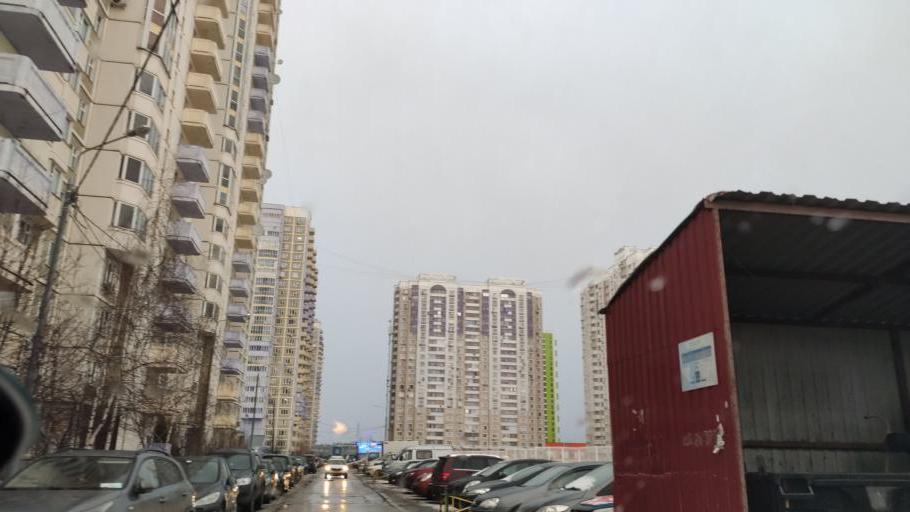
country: RU
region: Moscow
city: Khimki
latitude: 55.9045
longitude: 37.3940
